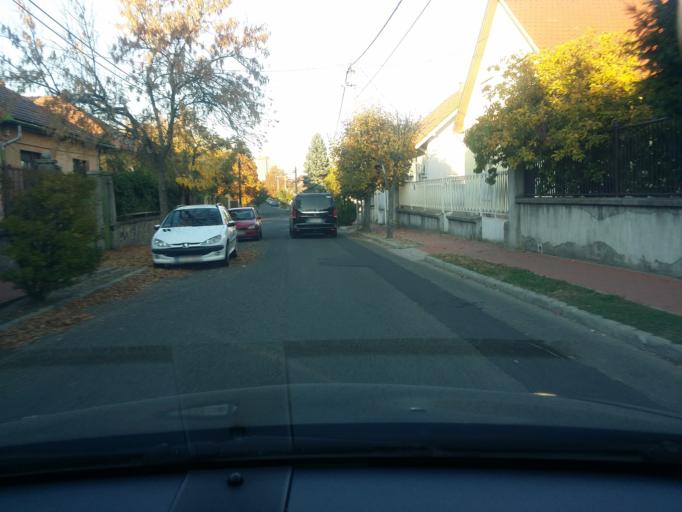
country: HU
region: Budapest
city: Budapest IV. keruelet
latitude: 47.5758
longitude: 19.0990
